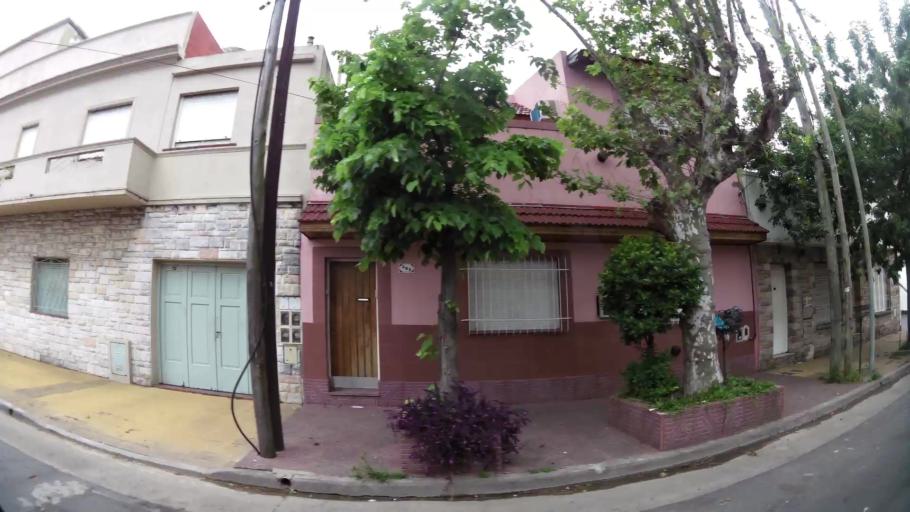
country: AR
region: Buenos Aires
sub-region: Partido de Avellaneda
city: Avellaneda
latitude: -34.6732
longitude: -58.3854
